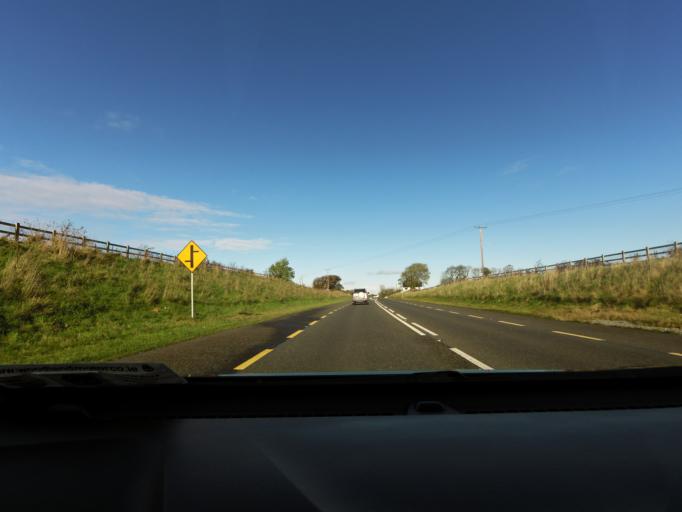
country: IE
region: Connaught
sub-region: County Galway
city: Claregalway
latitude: 53.4301
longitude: -9.0550
